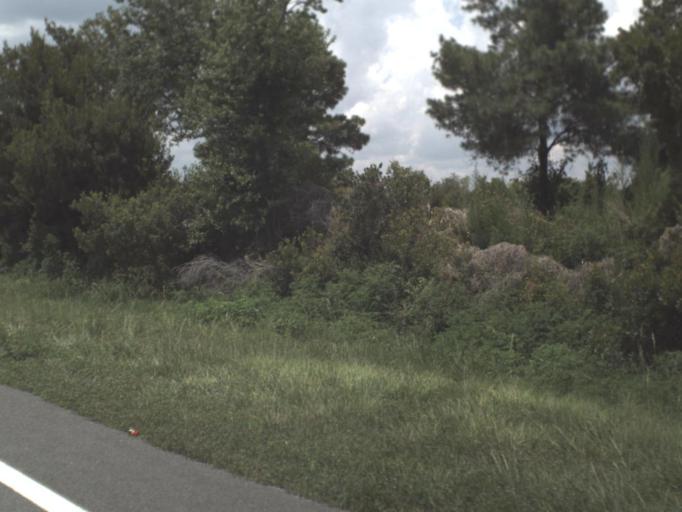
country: US
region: Florida
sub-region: Hamilton County
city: Jasper
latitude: 30.4524
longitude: -82.8884
